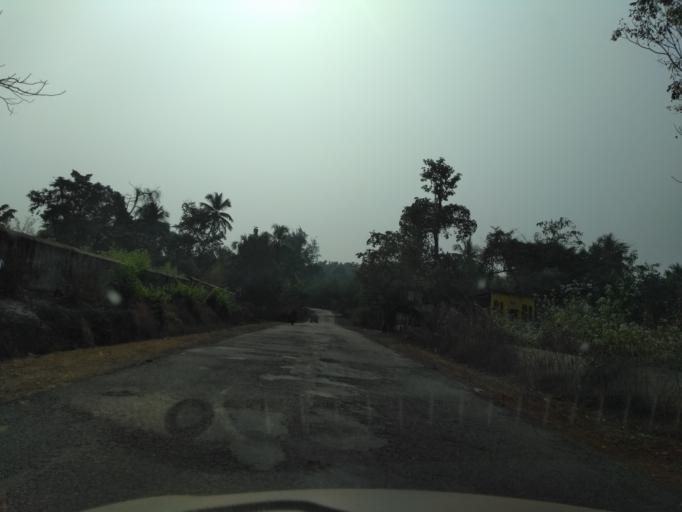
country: IN
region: Maharashtra
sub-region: Sindhudurg
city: Savantvadi
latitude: 15.8179
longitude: 73.9003
